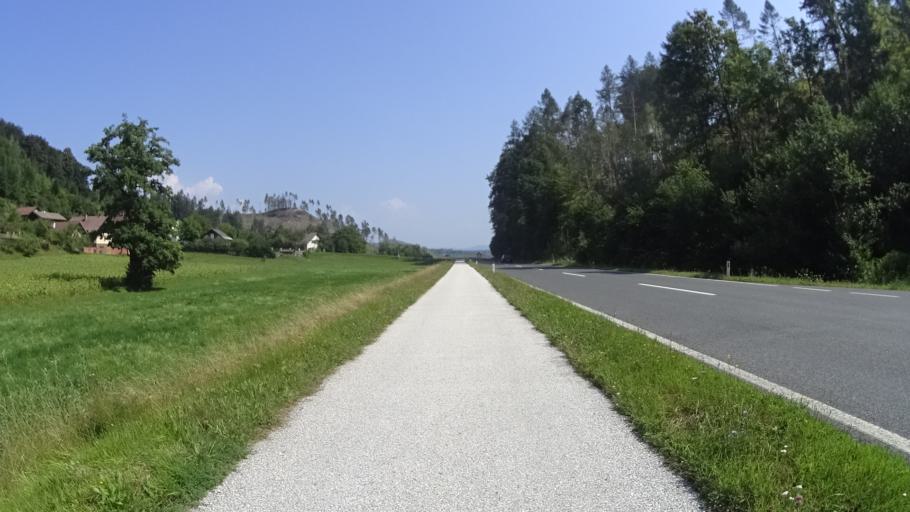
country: AT
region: Carinthia
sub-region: Politischer Bezirk Volkermarkt
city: Sittersdorf
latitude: 46.5535
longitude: 14.6118
